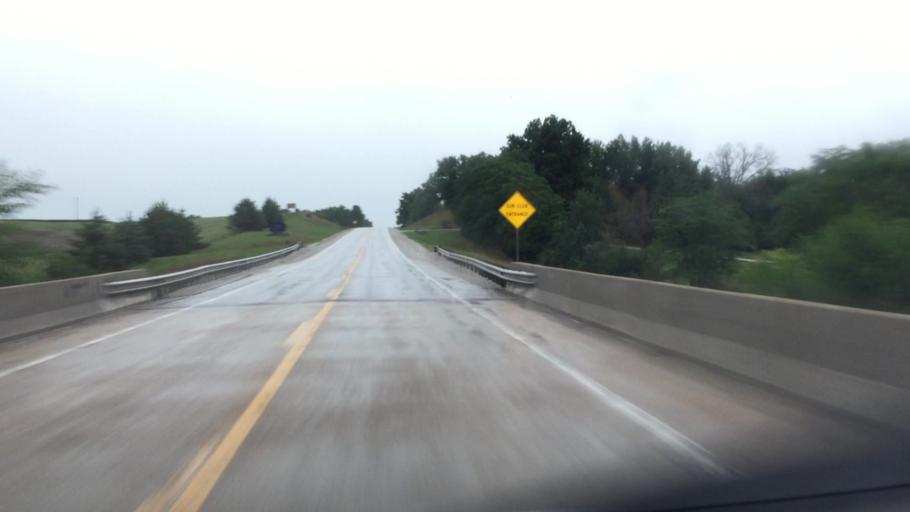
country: US
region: Illinois
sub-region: Hancock County
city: Carthage
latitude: 40.4307
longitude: -91.1401
